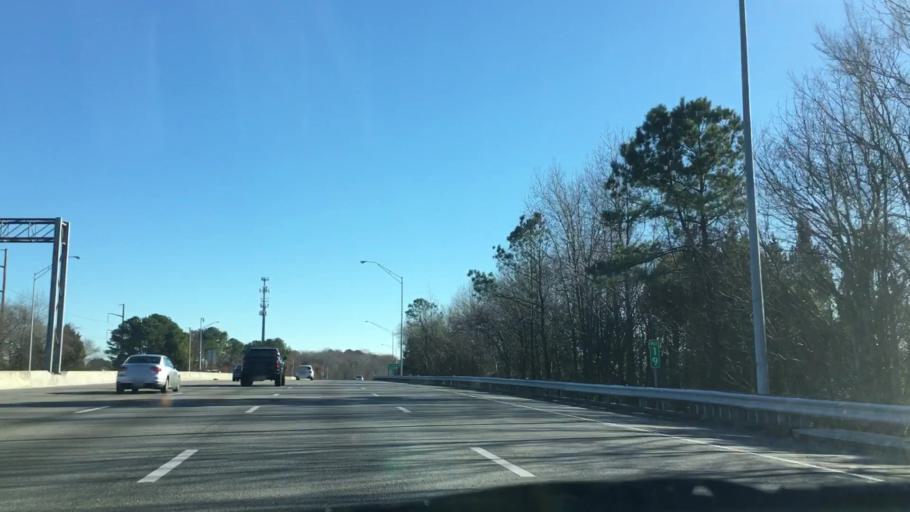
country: US
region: Virginia
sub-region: City of Virginia Beach
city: Virginia Beach
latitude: 36.8387
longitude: -76.0920
